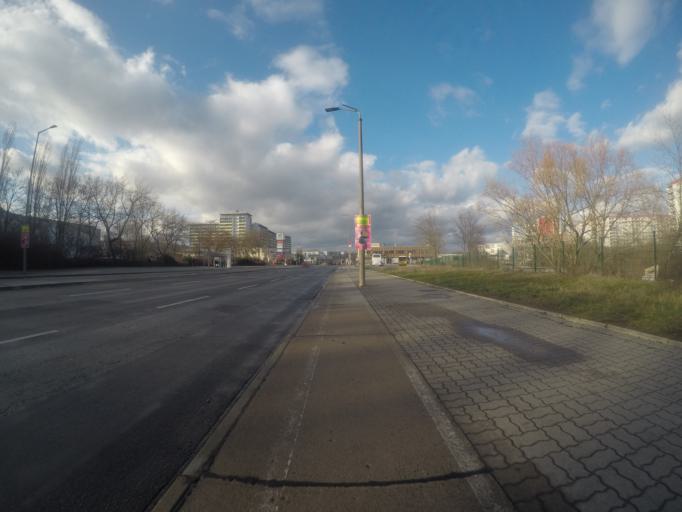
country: DE
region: Berlin
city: Kaulsdorf
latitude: 52.5197
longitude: 13.5886
